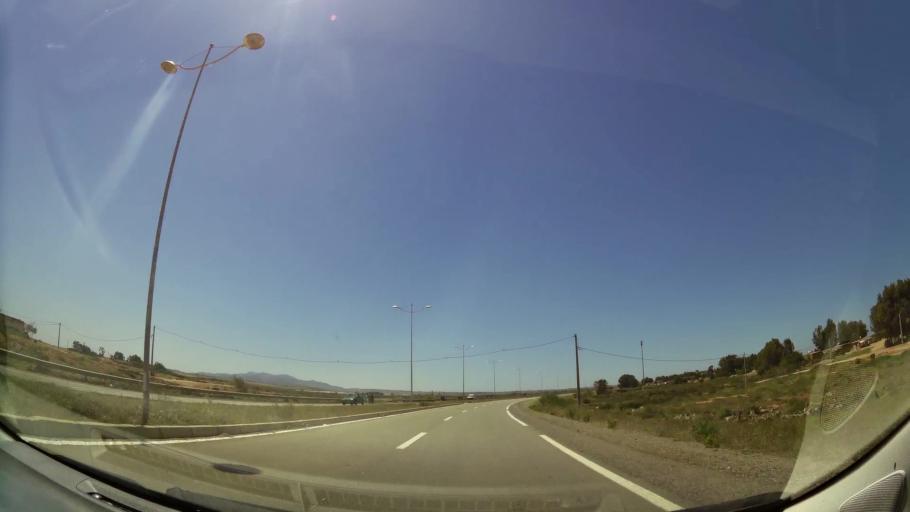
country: MA
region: Oriental
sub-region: Berkane-Taourirt
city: Madagh
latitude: 35.1001
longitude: -2.3313
